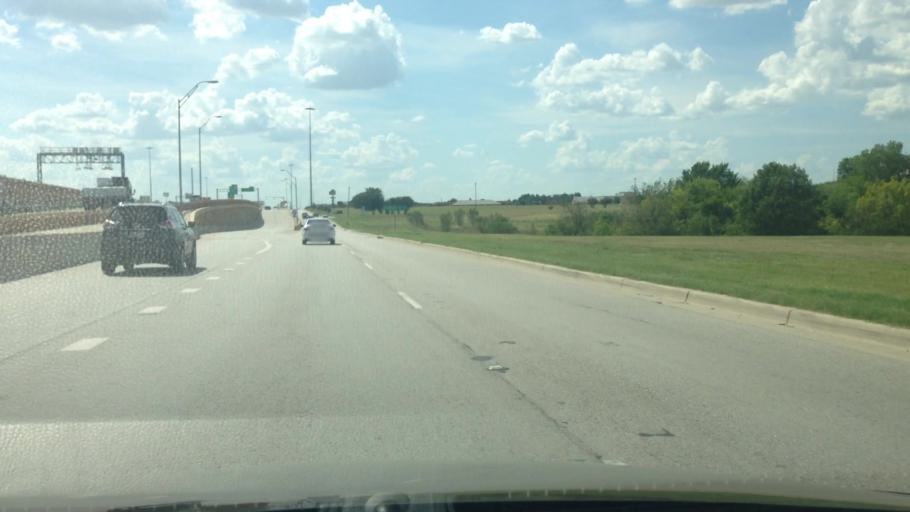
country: US
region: Texas
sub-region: Tarrant County
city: Watauga
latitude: 32.8401
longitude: -97.2821
